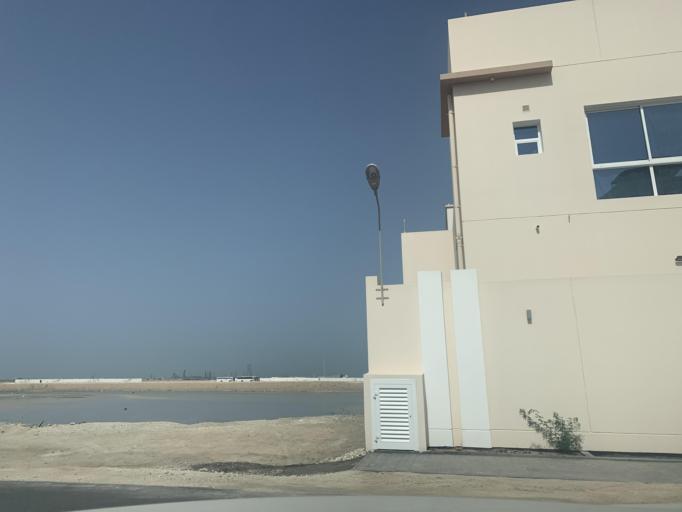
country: BH
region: Northern
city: Sitrah
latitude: 26.1673
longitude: 50.6283
